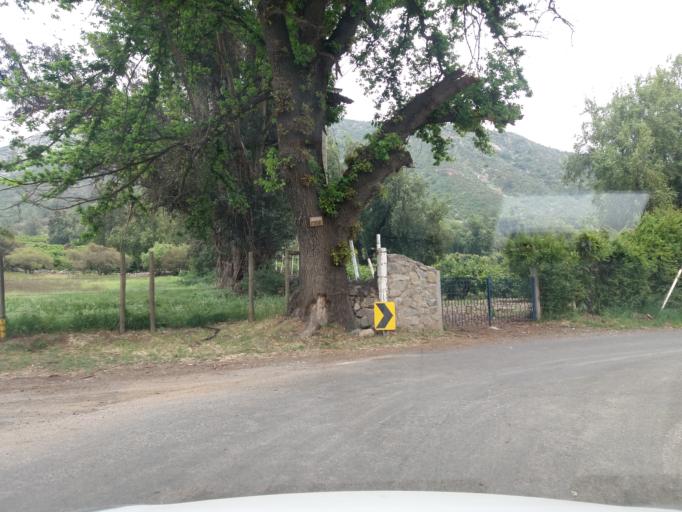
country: CL
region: Valparaiso
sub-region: Provincia de Quillota
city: Quillota
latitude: -32.9077
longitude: -71.1014
